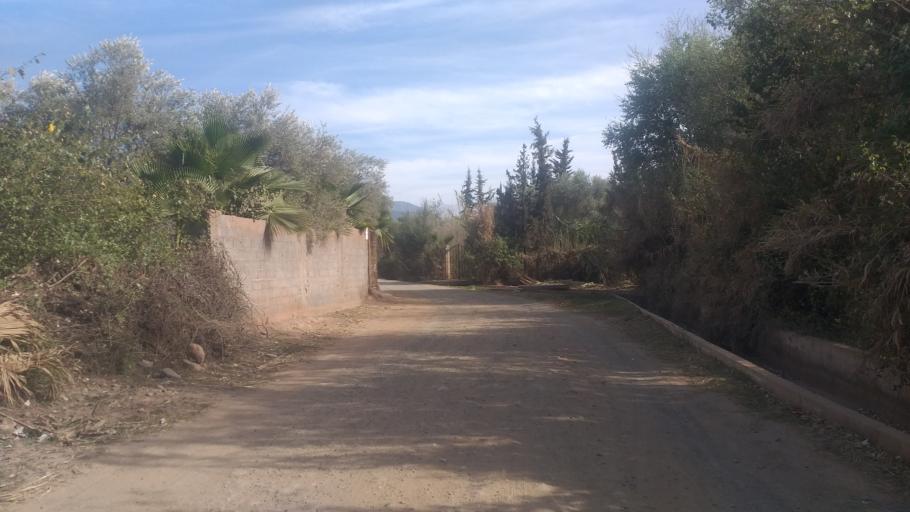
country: MA
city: Sidi Abdallah Ghiat
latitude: 31.4139
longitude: -7.7932
